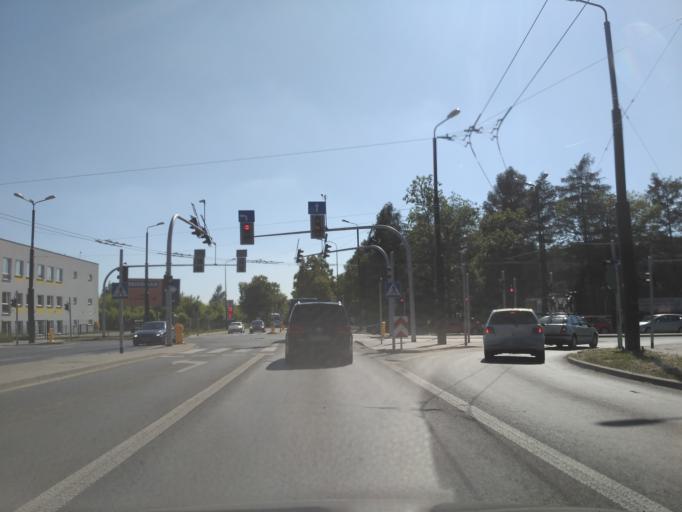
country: PL
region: Lublin Voivodeship
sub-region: Powiat lubelski
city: Lublin
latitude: 51.2032
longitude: 22.5605
